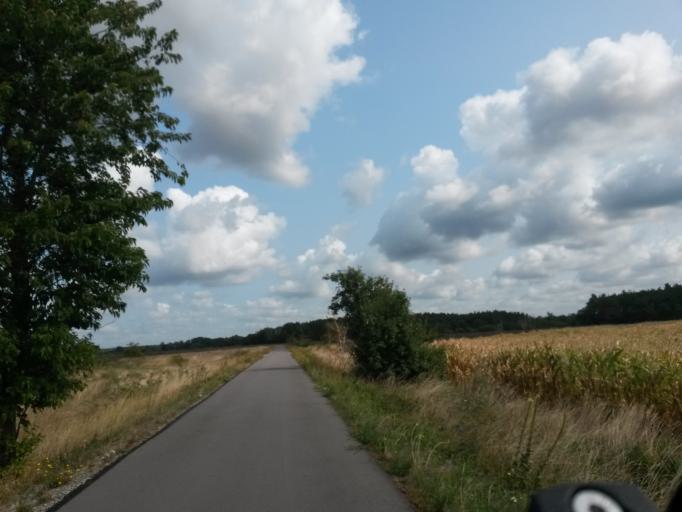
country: DE
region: Saxony-Anhalt
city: Klietz
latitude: 52.6590
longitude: 12.0527
